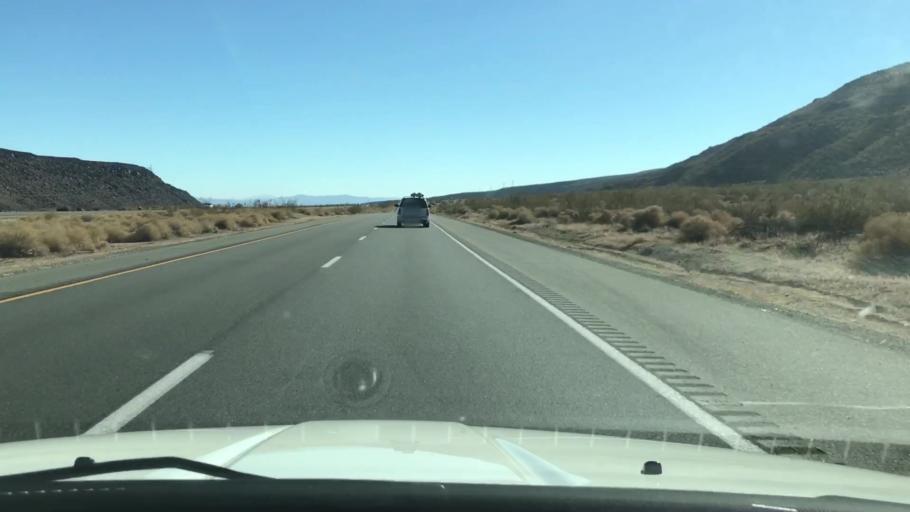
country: US
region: California
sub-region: Kern County
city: Inyokern
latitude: 35.9145
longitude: -117.9057
